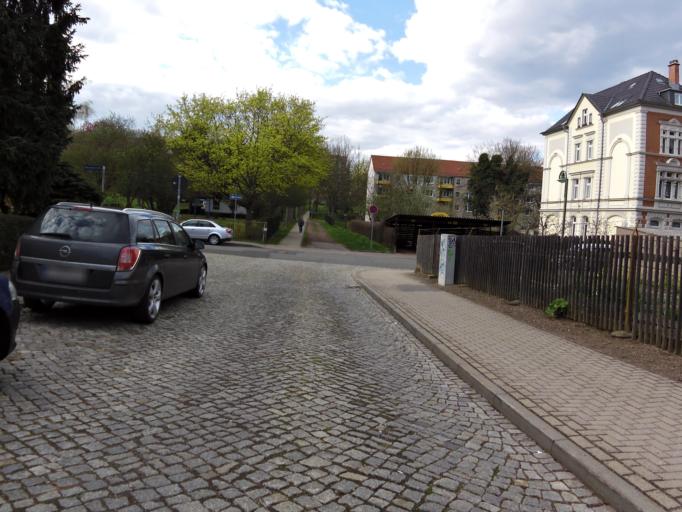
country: DE
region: Thuringia
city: Gotha
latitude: 50.9440
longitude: 10.6904
